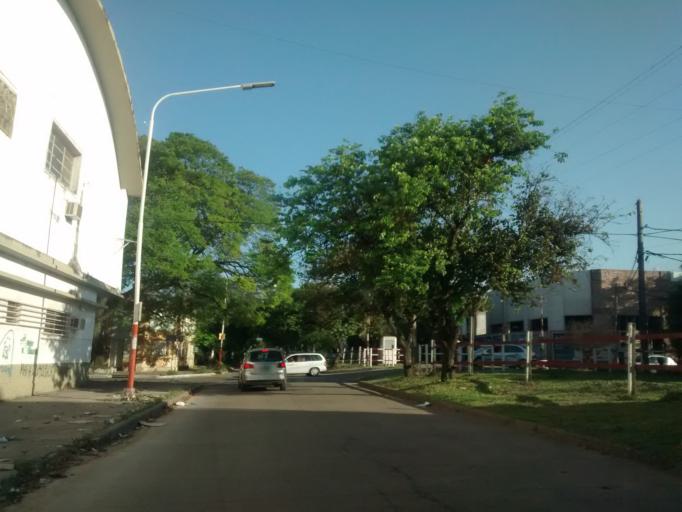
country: AR
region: Chaco
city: Resistencia
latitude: -27.4594
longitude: -58.9858
